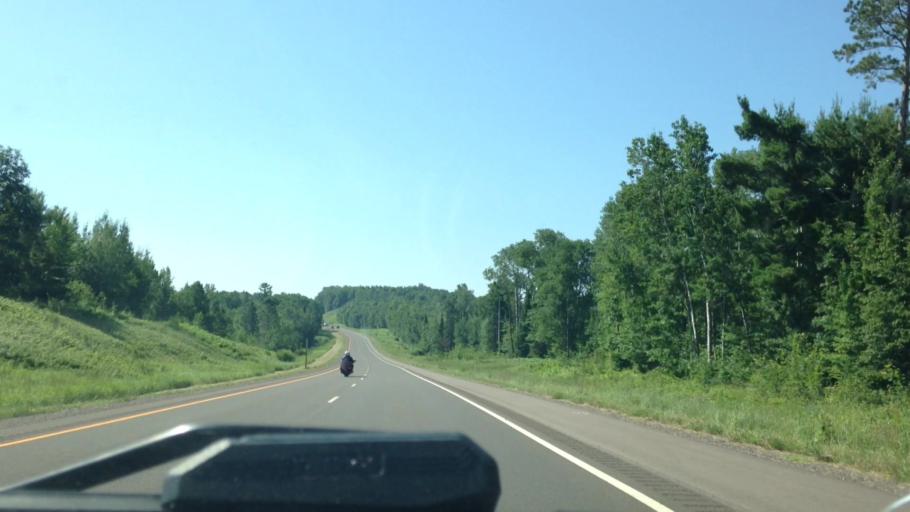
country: US
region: Wisconsin
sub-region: Washburn County
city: Spooner
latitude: 46.0158
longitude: -91.8379
